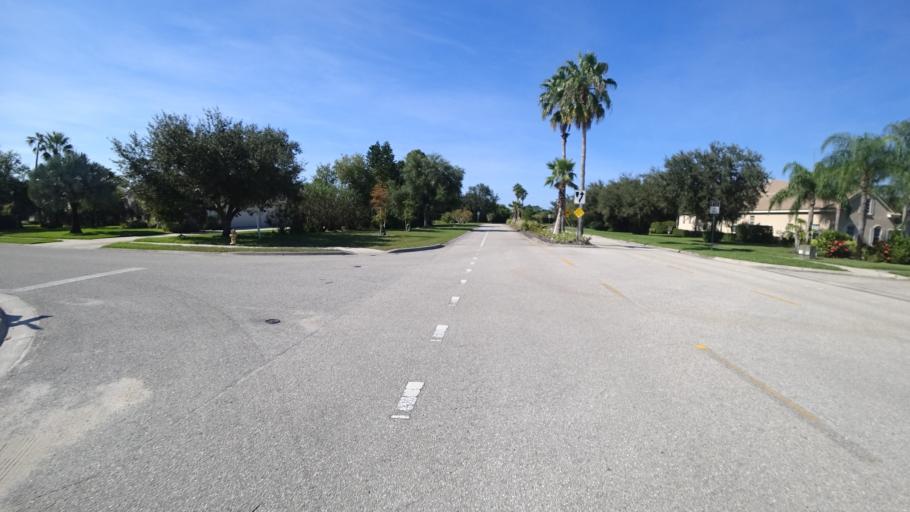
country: US
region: Florida
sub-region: Sarasota County
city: The Meadows
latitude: 27.4059
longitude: -82.4379
